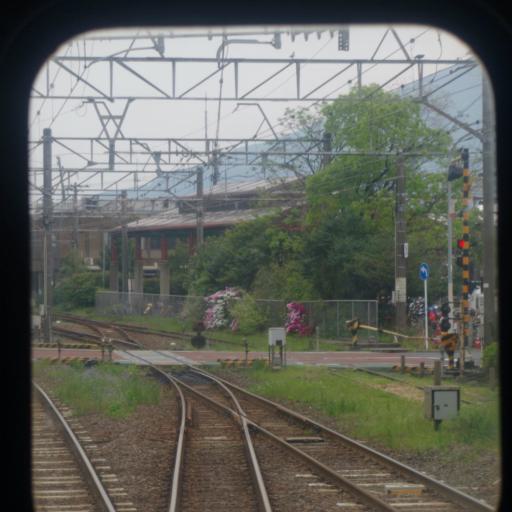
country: JP
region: Kagoshima
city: Kagoshima-shi
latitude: 31.6013
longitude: 130.5616
